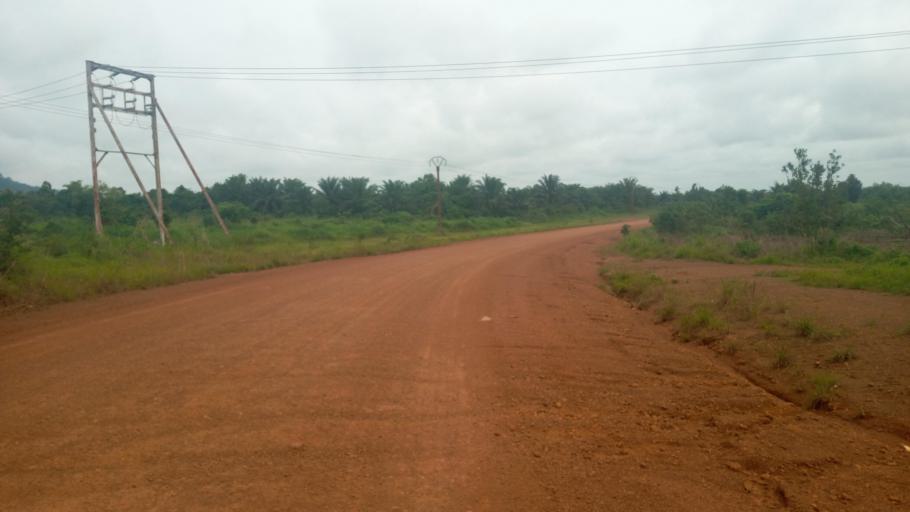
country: SL
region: Southern Province
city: Mogbwemo
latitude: 7.7412
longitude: -12.2886
